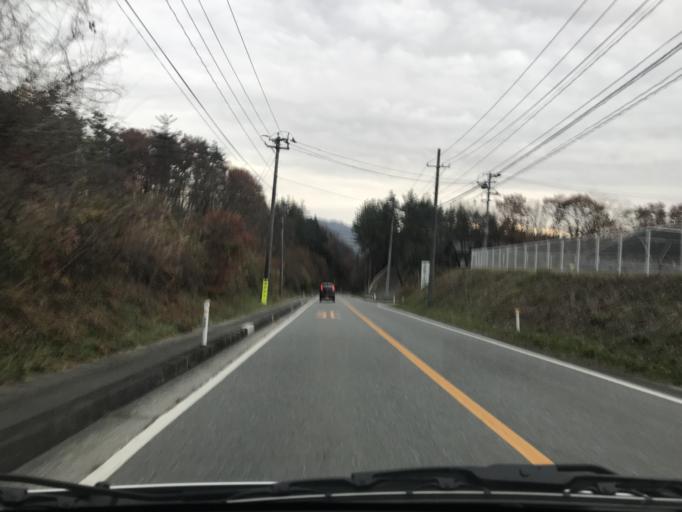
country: JP
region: Iwate
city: Ichinoseki
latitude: 39.0033
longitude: 141.3254
